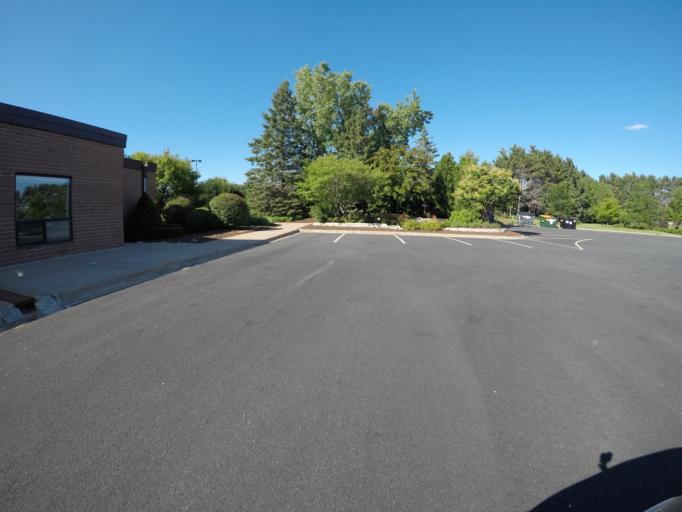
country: US
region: Minnesota
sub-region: Hennepin County
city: Maple Grove
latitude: 45.0853
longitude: -93.4296
